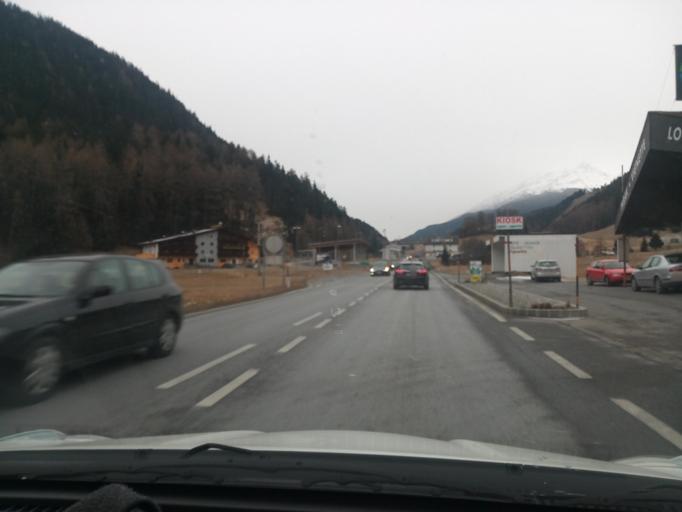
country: AT
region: Tyrol
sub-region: Politischer Bezirk Landeck
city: Nauders
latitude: 46.8508
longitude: 10.5047
